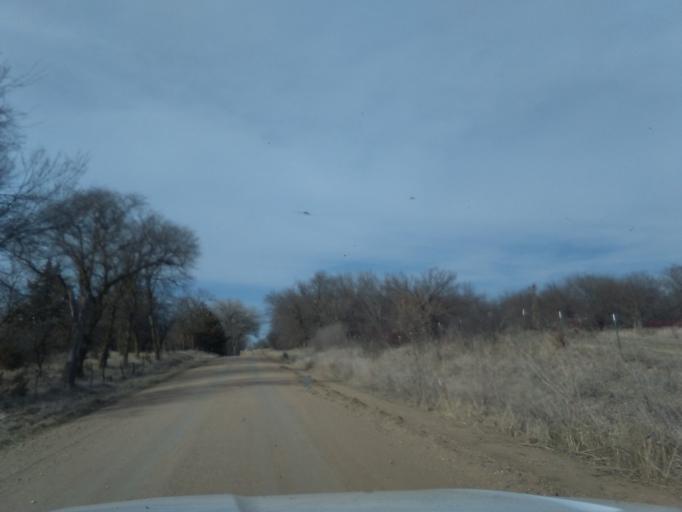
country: US
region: Nebraska
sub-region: Jefferson County
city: Fairbury
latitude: 40.2061
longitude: -97.2365
